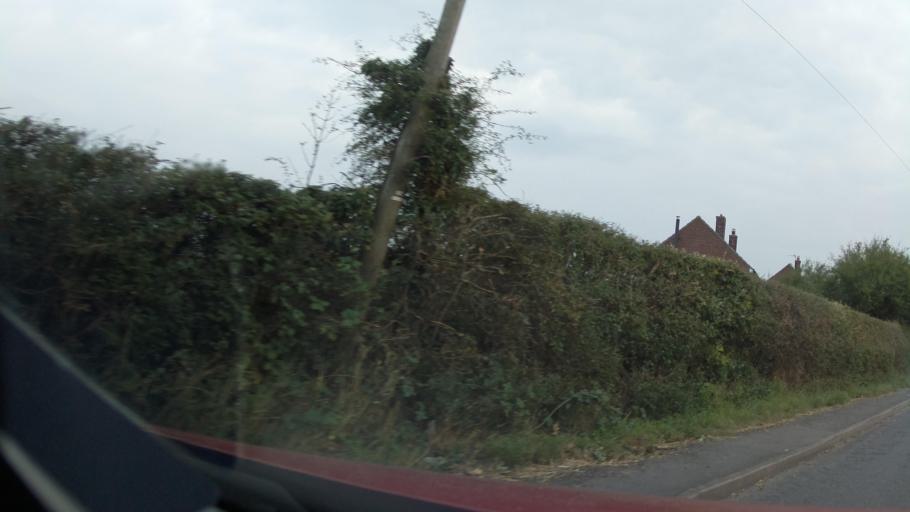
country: GB
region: England
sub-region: Lincolnshire
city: Skellingthorpe
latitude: 53.1408
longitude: -0.6458
